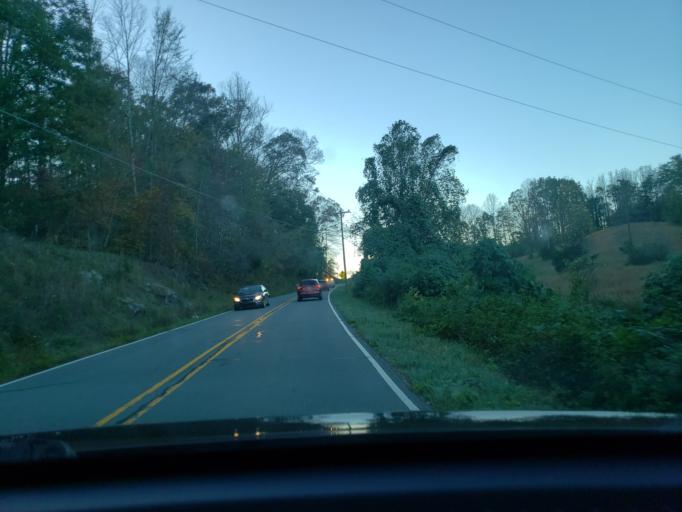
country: US
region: North Carolina
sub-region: Stokes County
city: Danbury
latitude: 36.4245
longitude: -80.2380
